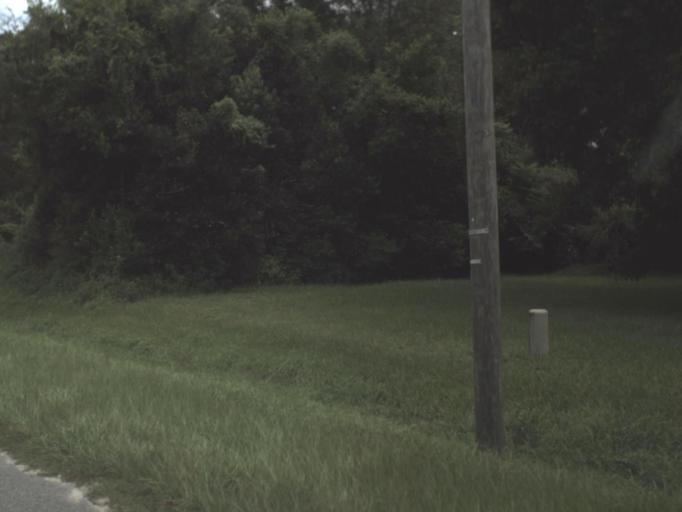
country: US
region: Florida
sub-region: Pasco County
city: Dade City
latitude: 28.3627
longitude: -82.2040
